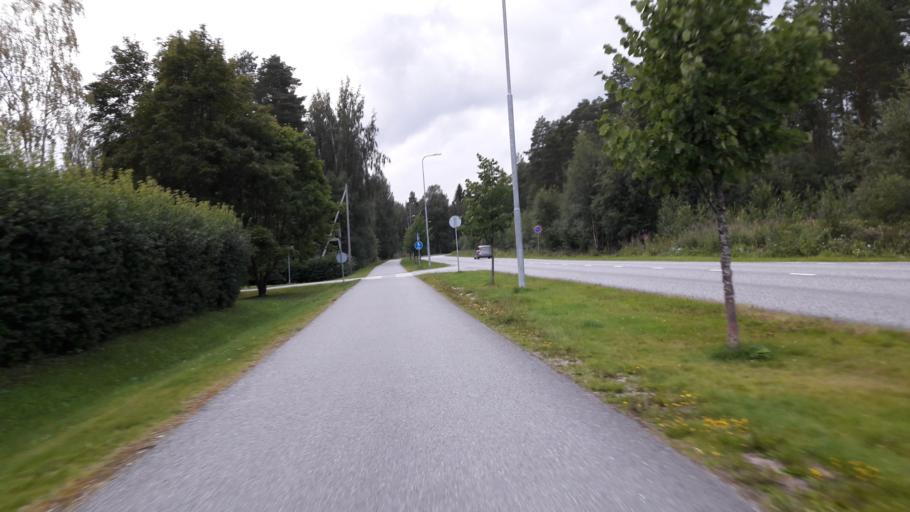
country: FI
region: North Karelia
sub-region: Joensuu
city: Joensuu
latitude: 62.5374
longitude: 29.8350
